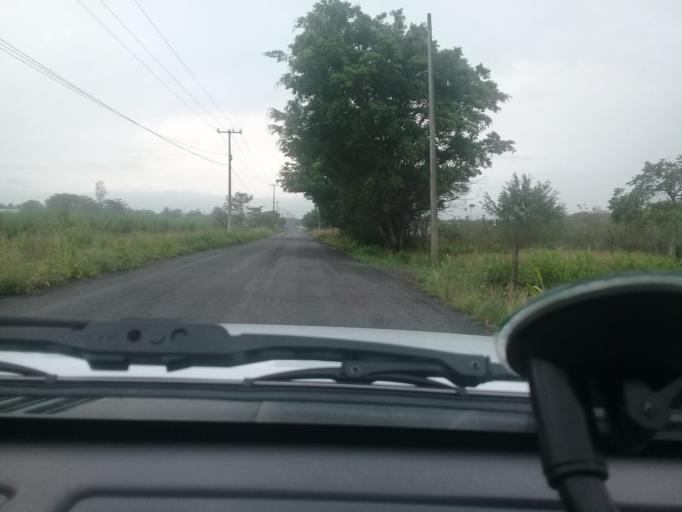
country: MX
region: Veracruz
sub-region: La Antigua
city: Nicolas Blanco (San Pancho)
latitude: 19.3574
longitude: -96.3542
